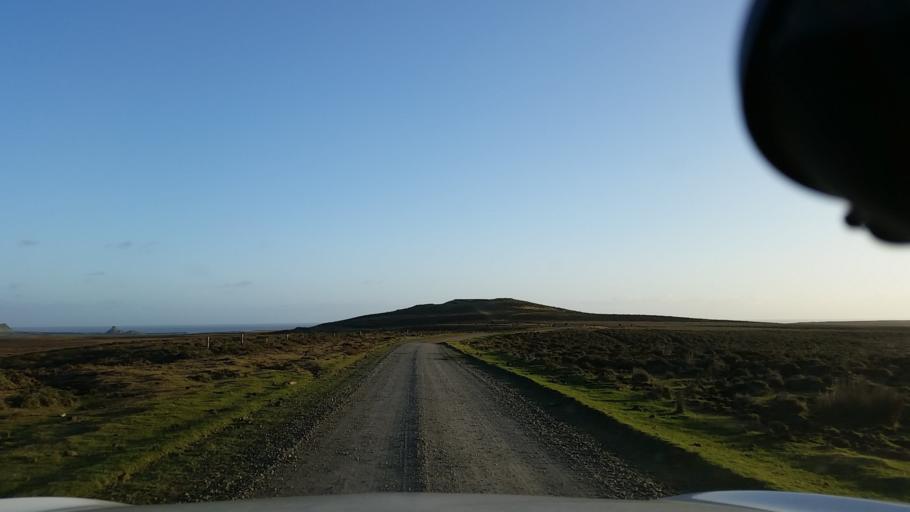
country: NZ
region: Chatham Islands
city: Waitangi
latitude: -43.7906
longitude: -176.7236
